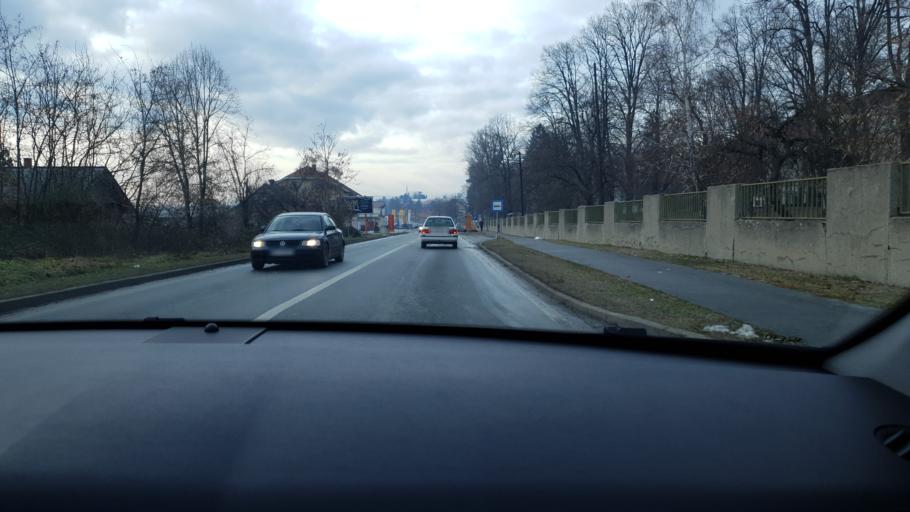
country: HR
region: Pozesko-Slavonska
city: Pozega
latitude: 45.3425
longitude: 17.6996
